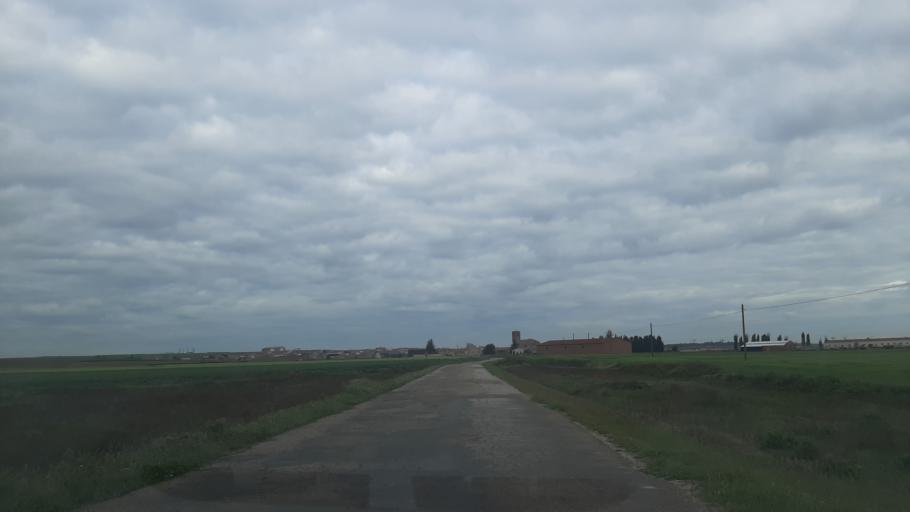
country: ES
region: Castille and Leon
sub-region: Provincia de Salamanca
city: Villaflores
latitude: 41.0815
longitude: -5.2229
